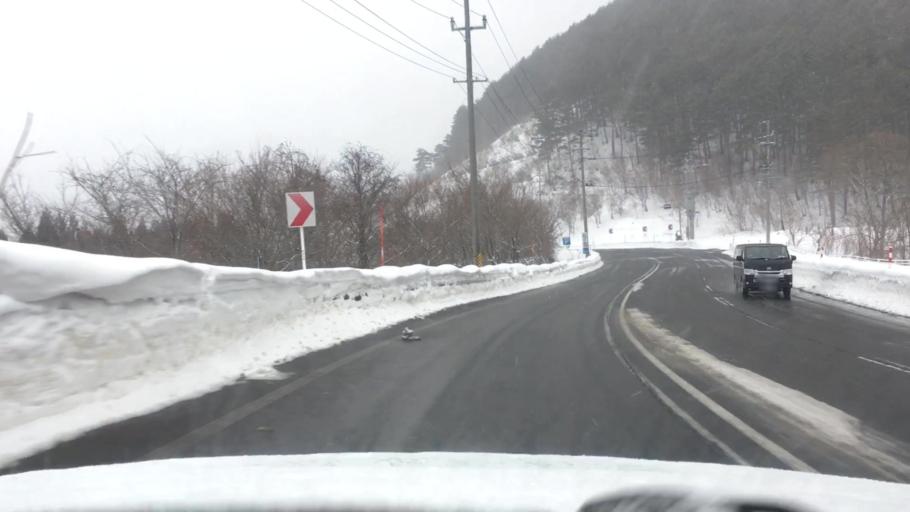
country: JP
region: Akita
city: Hanawa
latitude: 40.0232
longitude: 140.9863
